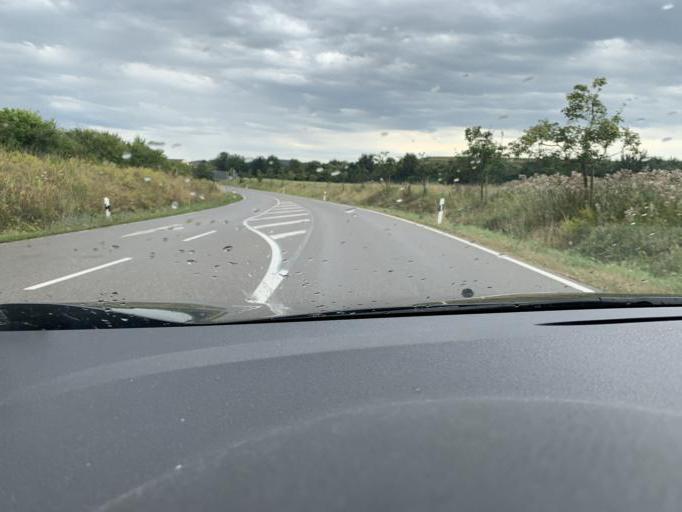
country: DE
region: Baden-Wuerttemberg
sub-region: Regierungsbezirk Stuttgart
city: Schwaebisch Hall
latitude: 49.1190
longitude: 9.7690
